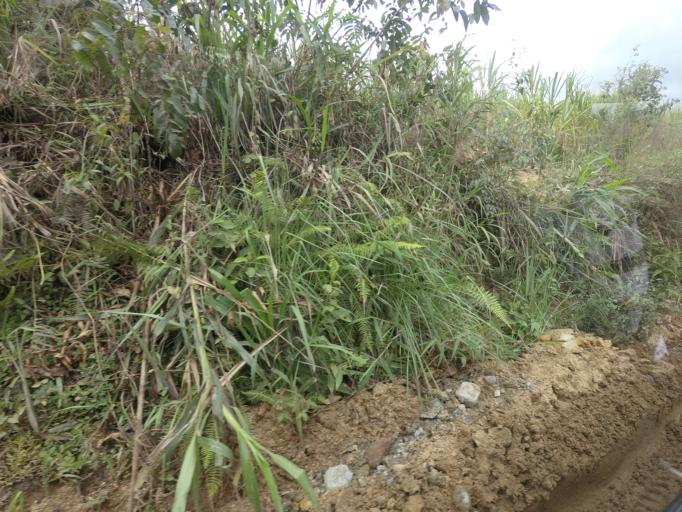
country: CO
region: Huila
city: San Agustin
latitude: 1.9561
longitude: -76.2976
